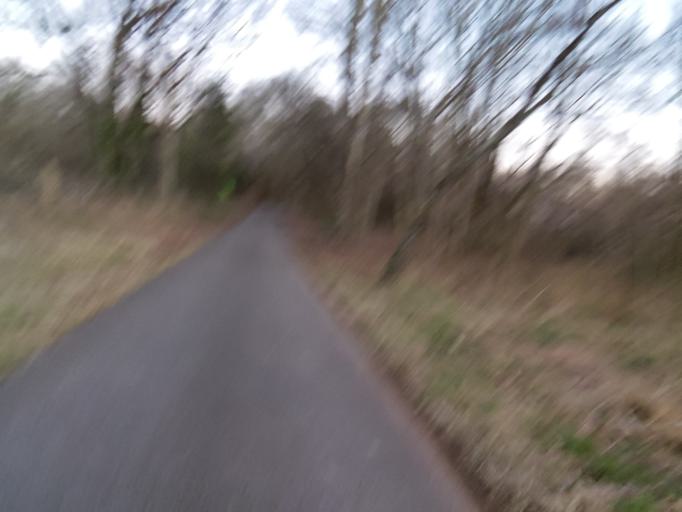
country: US
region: Tennessee
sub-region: Knox County
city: Knoxville
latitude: 35.9554
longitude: -83.8674
